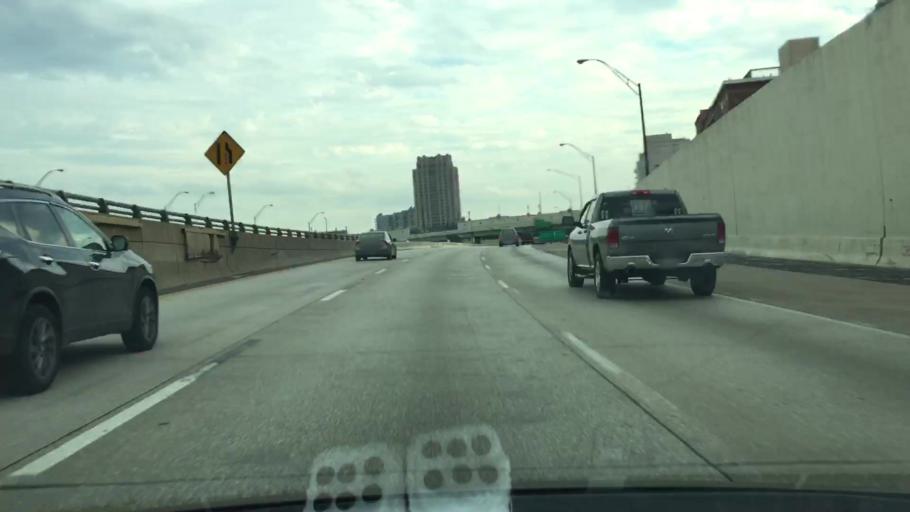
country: US
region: Pennsylvania
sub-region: Philadelphia County
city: Philadelphia
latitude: 39.9521
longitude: -75.1428
